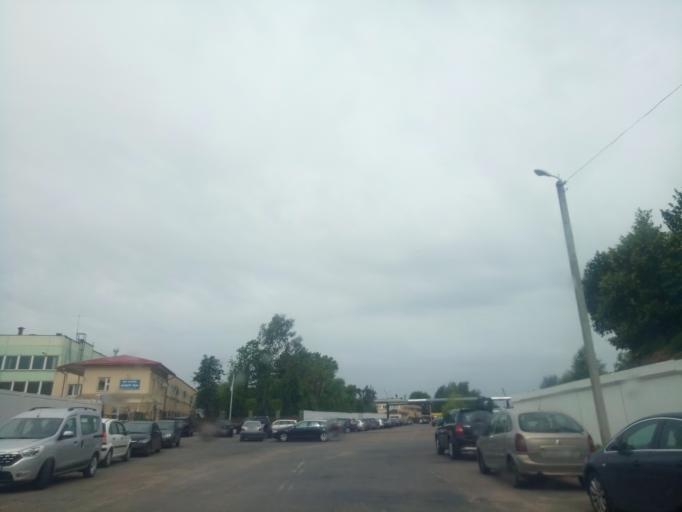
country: BY
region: Minsk
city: Novoye Medvezhino
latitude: 53.8861
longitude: 27.4952
